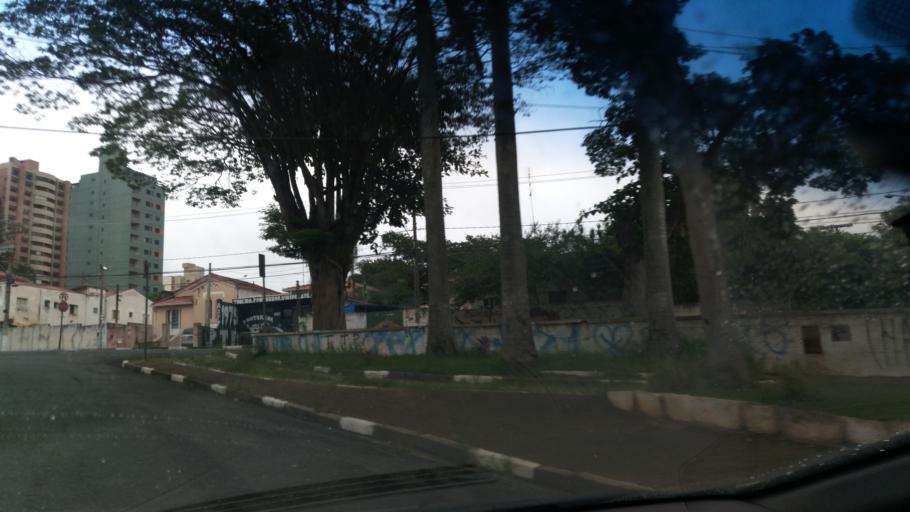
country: BR
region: Sao Paulo
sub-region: Campinas
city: Campinas
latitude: -22.9122
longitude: -47.0502
